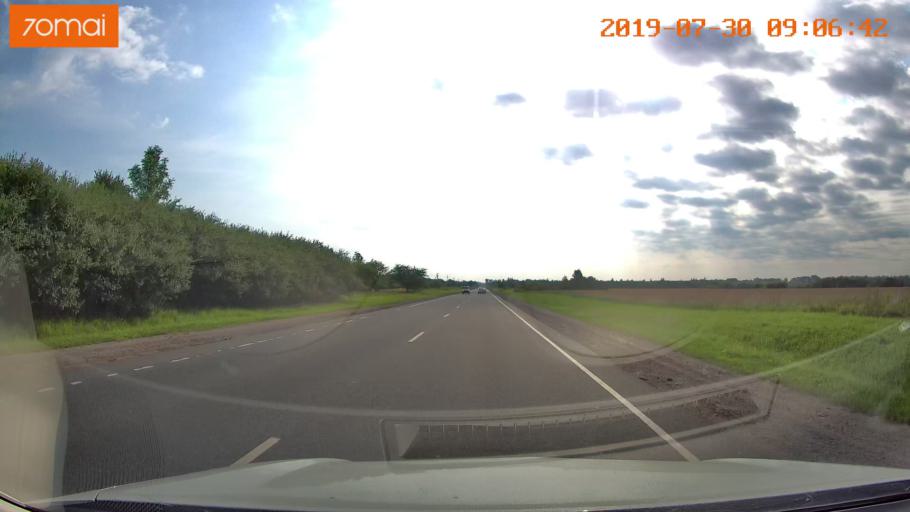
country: RU
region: Kaliningrad
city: Gusev
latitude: 54.6100
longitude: 22.3436
